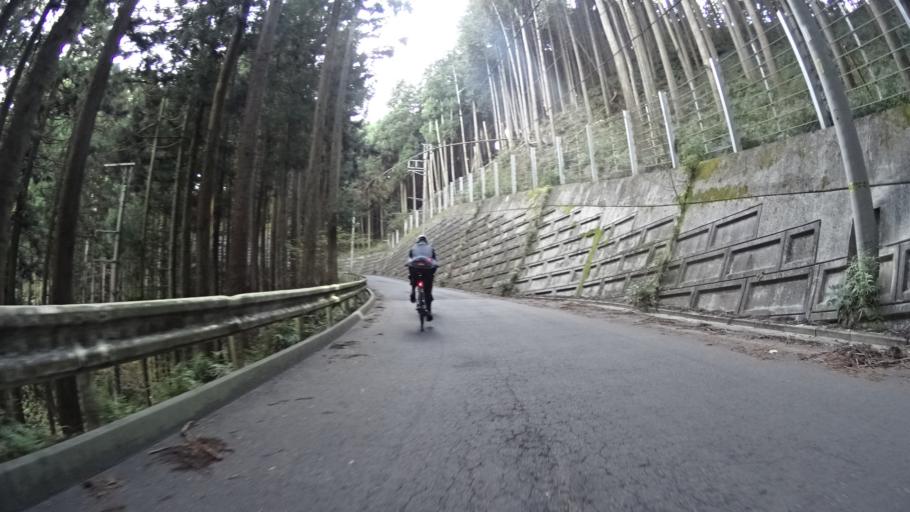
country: JP
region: Saitama
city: Chichibu
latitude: 35.9148
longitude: 139.1767
